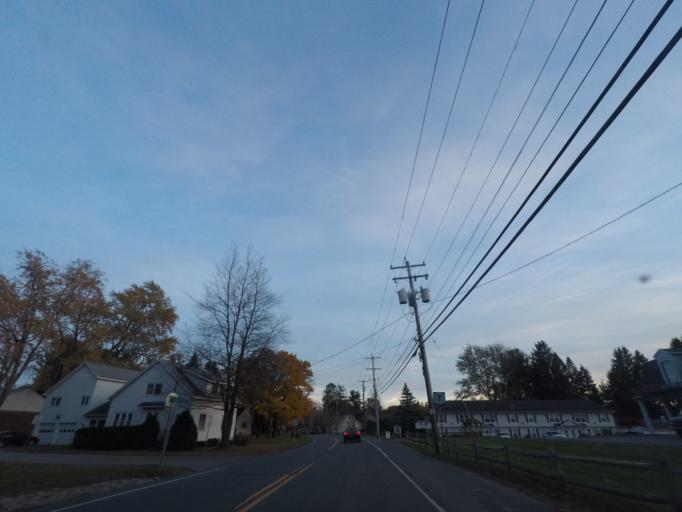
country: US
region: New York
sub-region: Schenectady County
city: Rotterdam
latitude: 42.7749
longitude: -73.9524
